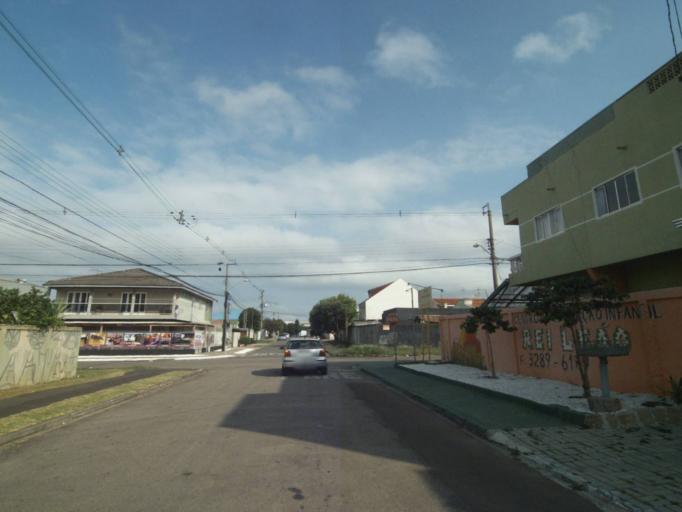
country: BR
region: Parana
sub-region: Sao Jose Dos Pinhais
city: Sao Jose dos Pinhais
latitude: -25.5361
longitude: -49.2578
